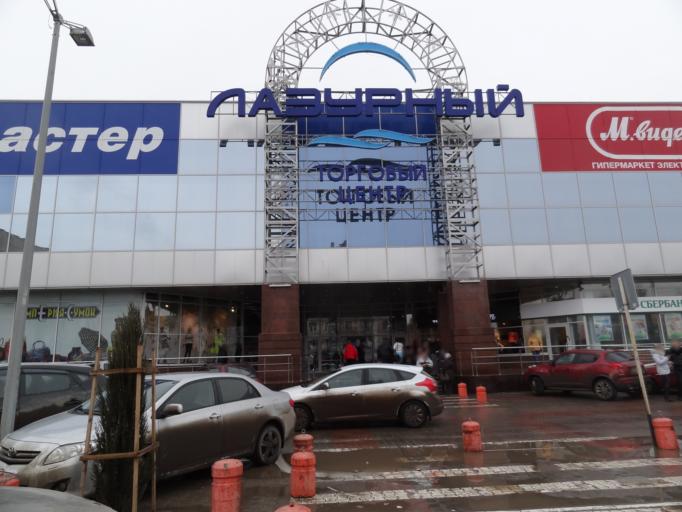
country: RU
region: Saratov
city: Engel's
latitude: 51.5031
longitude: 46.1187
